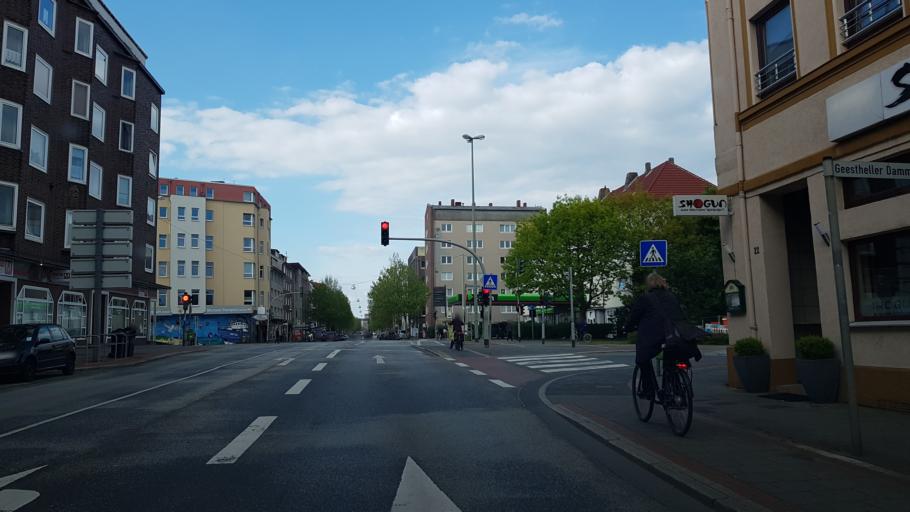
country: DE
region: Bremen
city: Bremerhaven
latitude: 53.5508
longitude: 8.5804
